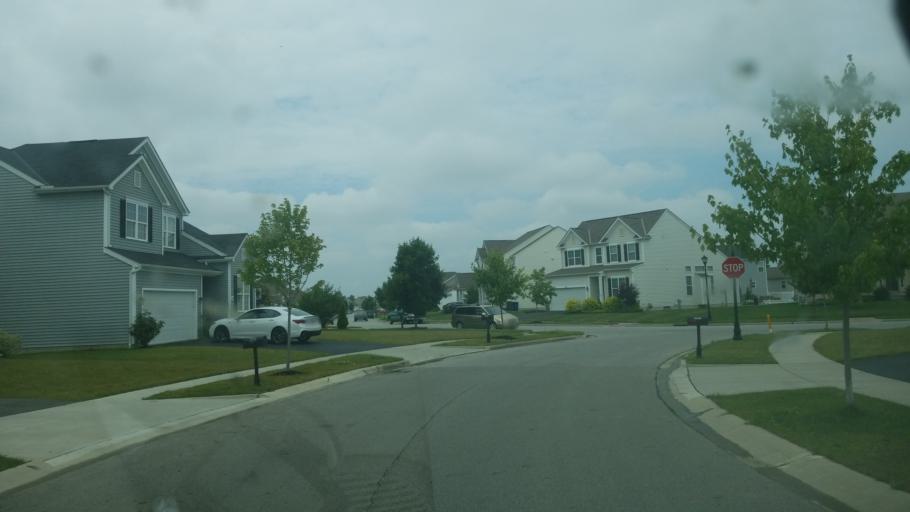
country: US
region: Ohio
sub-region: Franklin County
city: Reynoldsburg
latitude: 39.9990
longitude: -82.7758
